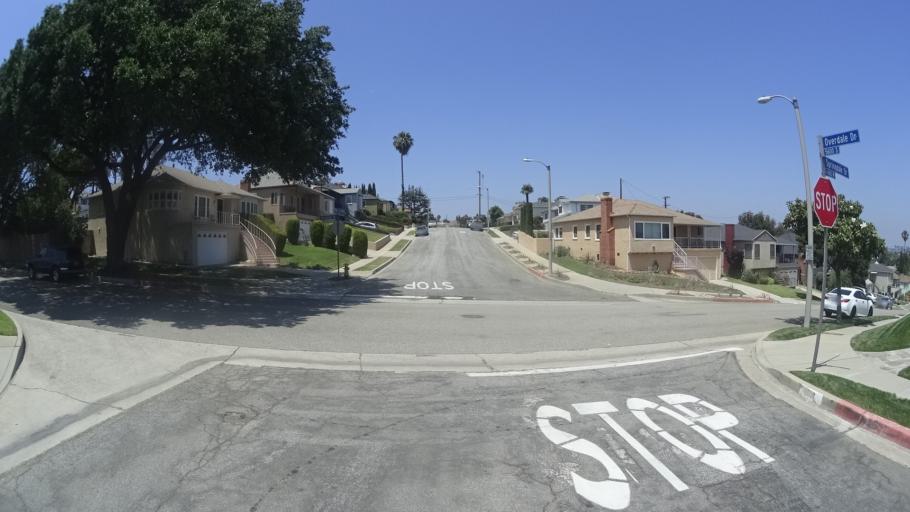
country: US
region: California
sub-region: Los Angeles County
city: View Park-Windsor Hills
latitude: 33.9904
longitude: -118.3532
